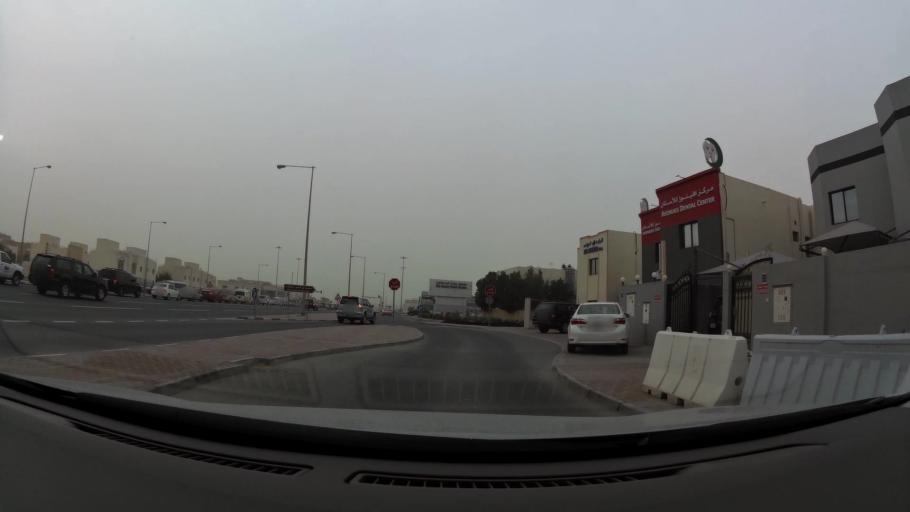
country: QA
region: Baladiyat ad Dawhah
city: Doha
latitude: 25.2371
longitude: 51.4995
